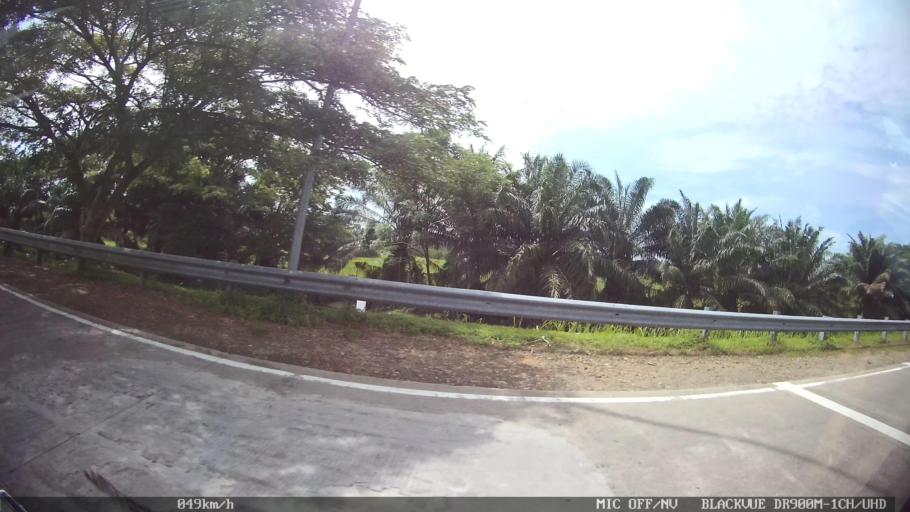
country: ID
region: North Sumatra
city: Percut
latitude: 3.6307
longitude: 98.8771
